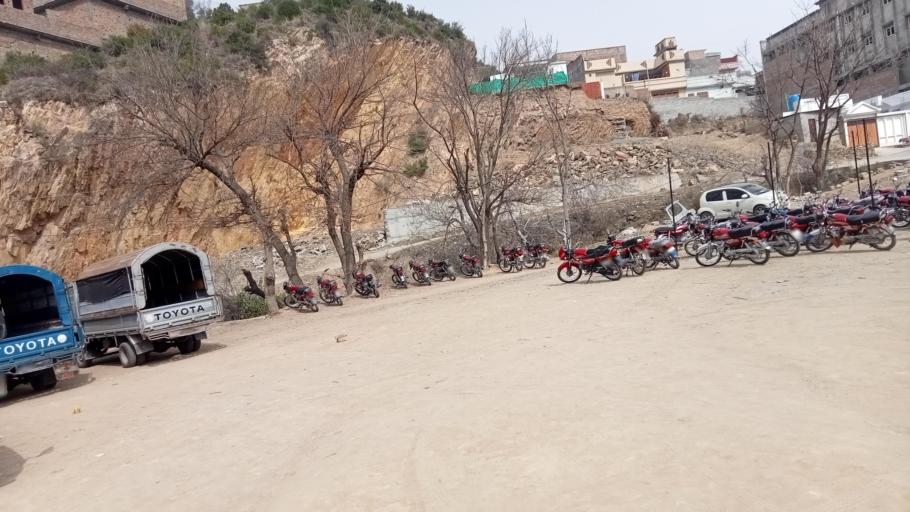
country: PK
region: Khyber Pakhtunkhwa
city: Mingora
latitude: 34.7609
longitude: 72.3827
